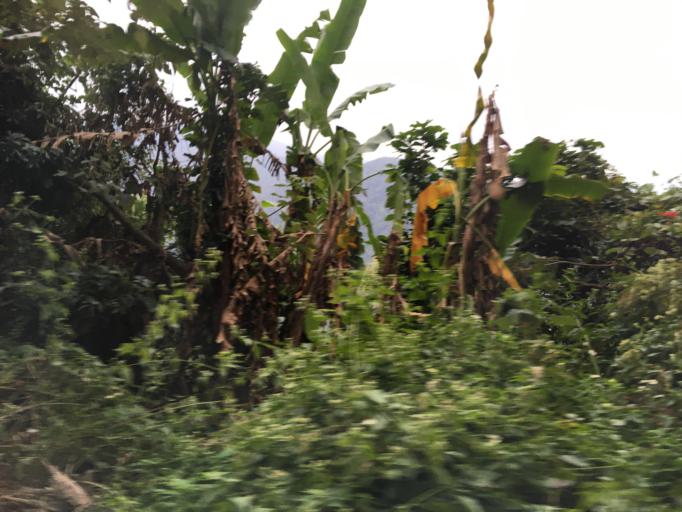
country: TW
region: Taiwan
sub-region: Chiayi
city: Jiayi Shi
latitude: 23.5365
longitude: 120.6094
